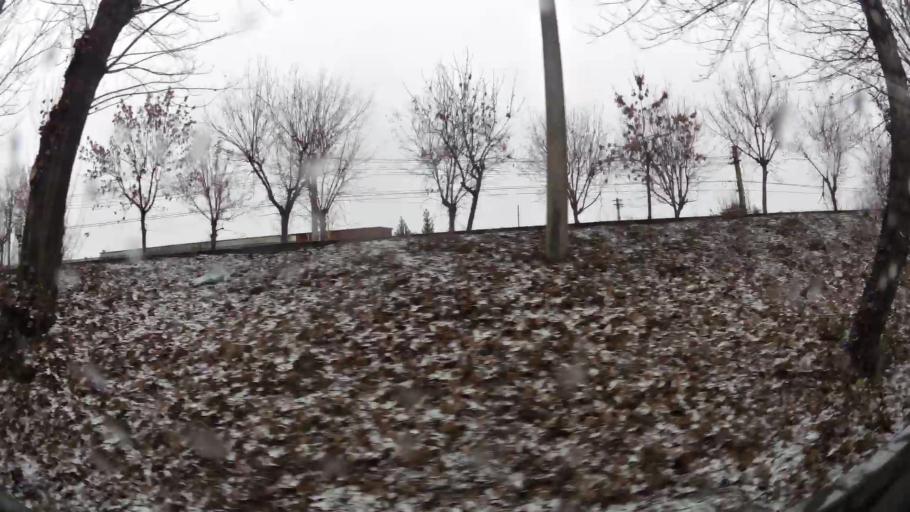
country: RO
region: Dambovita
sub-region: Municipiul Targoviste
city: Targoviste
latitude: 44.9108
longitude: 25.4544
